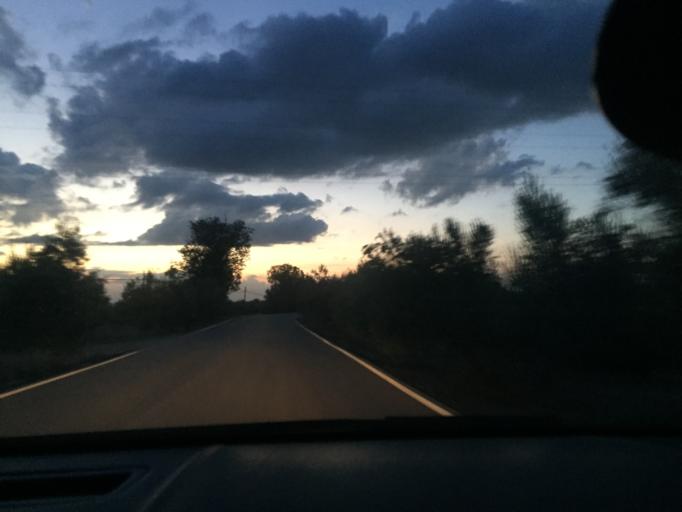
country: ES
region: Andalusia
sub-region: Provincia de Jaen
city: Mancha Real
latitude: 37.7904
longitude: -3.6260
